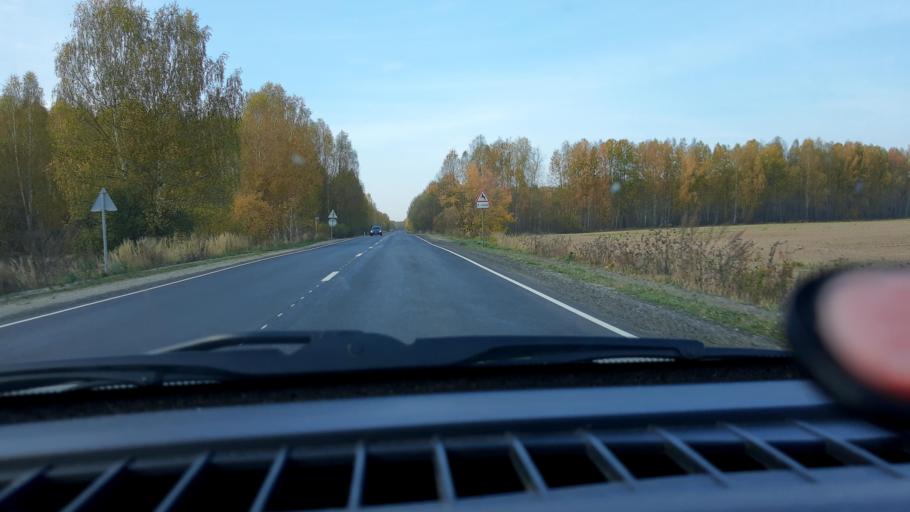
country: RU
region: Nizjnij Novgorod
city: Lukino
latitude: 56.5353
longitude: 43.7886
